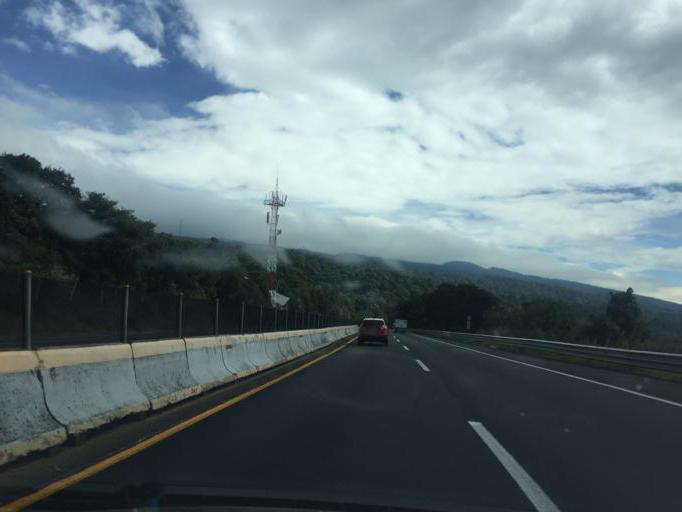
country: MX
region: Morelos
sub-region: Cuernavaca
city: Villa Santiago
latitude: 19.0257
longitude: -99.1864
